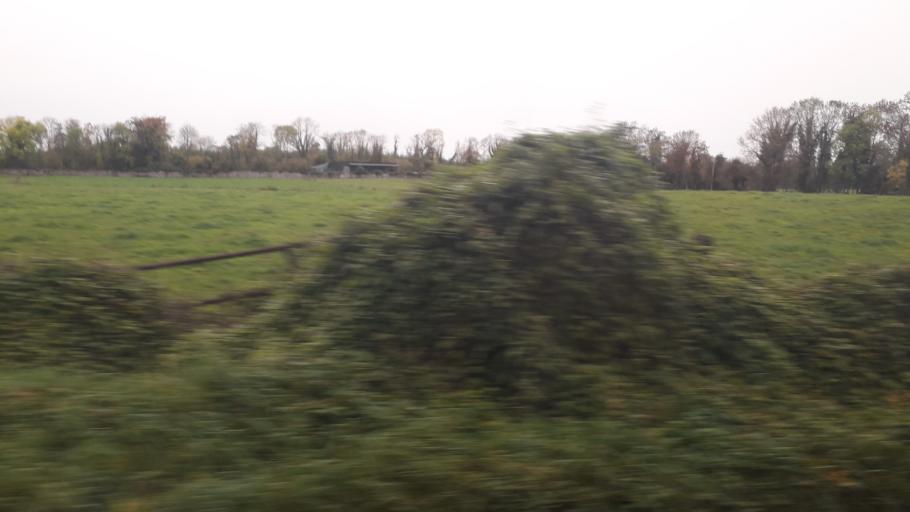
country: IE
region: Leinster
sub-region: Uibh Fhaili
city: Birr
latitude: 52.9771
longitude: -7.9447
